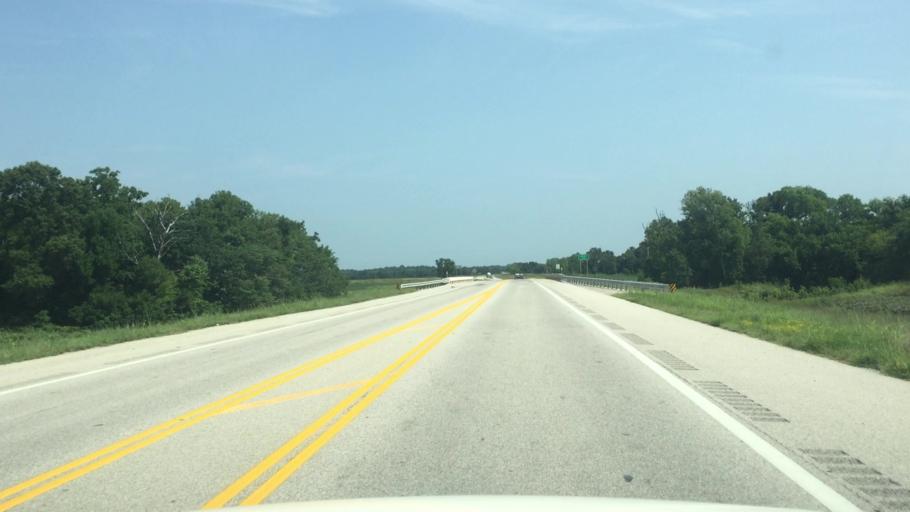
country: US
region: Kansas
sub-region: Montgomery County
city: Coffeyville
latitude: 37.1134
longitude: -95.5844
